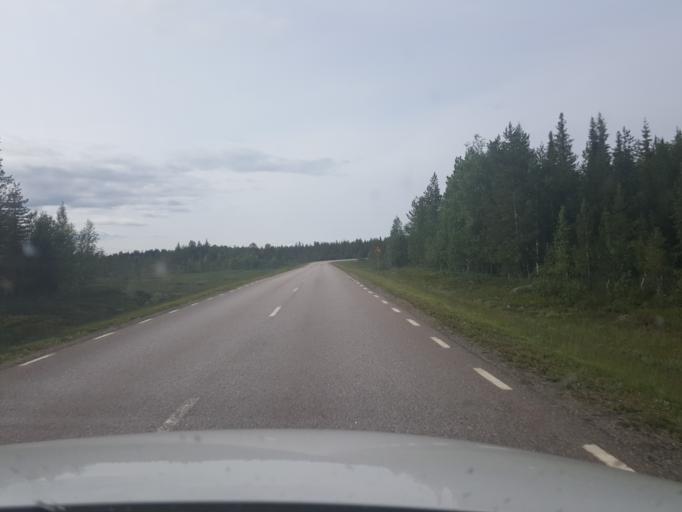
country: SE
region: Norrbotten
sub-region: Arjeplogs Kommun
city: Arjeplog
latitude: 65.7265
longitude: 18.0633
